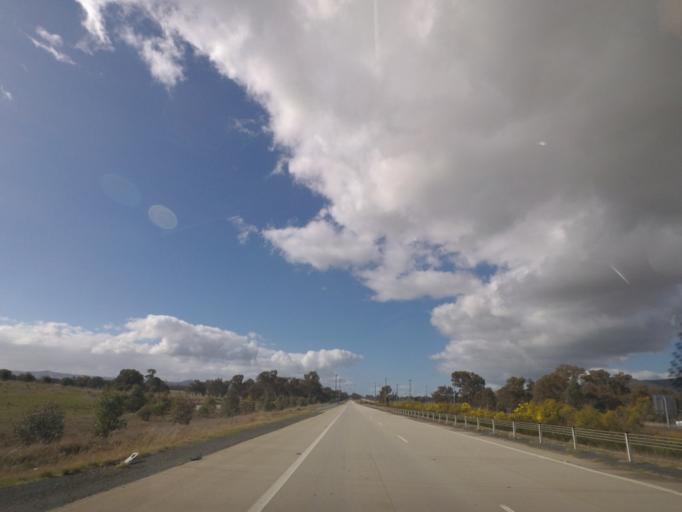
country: AU
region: New South Wales
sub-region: Greater Hume Shire
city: Holbrook
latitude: -35.6972
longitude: 147.3388
